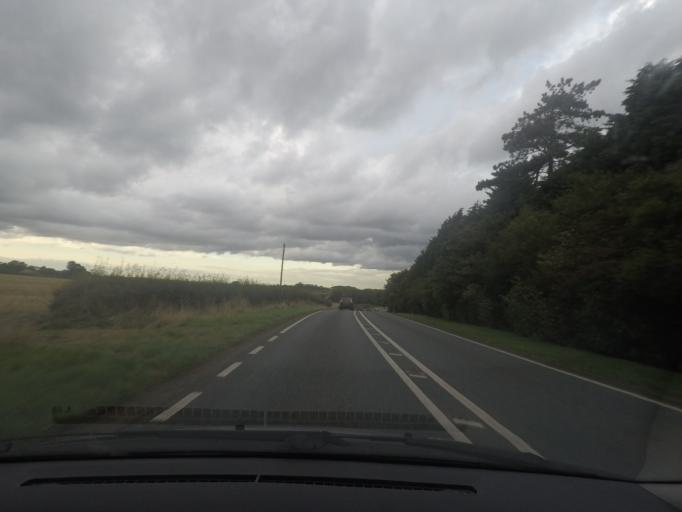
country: GB
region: England
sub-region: Lincolnshire
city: Louth
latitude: 53.3300
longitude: 0.0082
